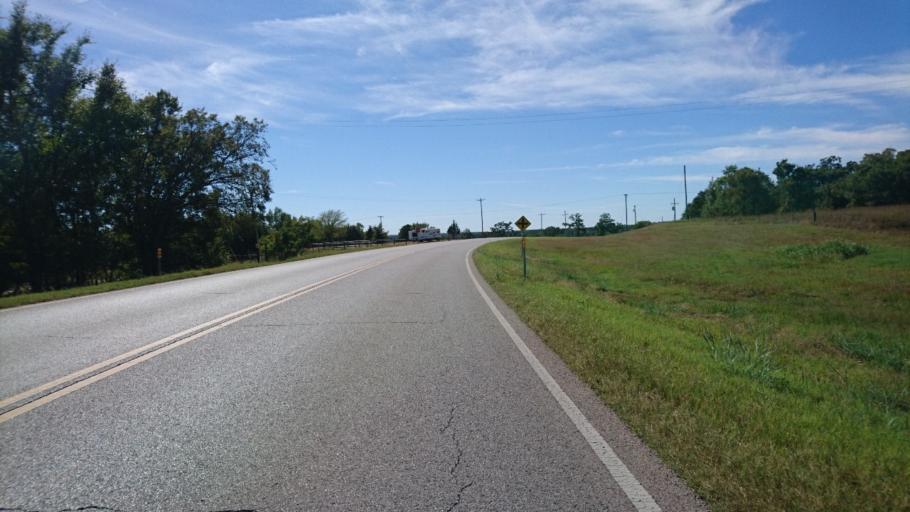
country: US
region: Oklahoma
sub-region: Lincoln County
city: Stroud
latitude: 35.7246
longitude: -96.7315
